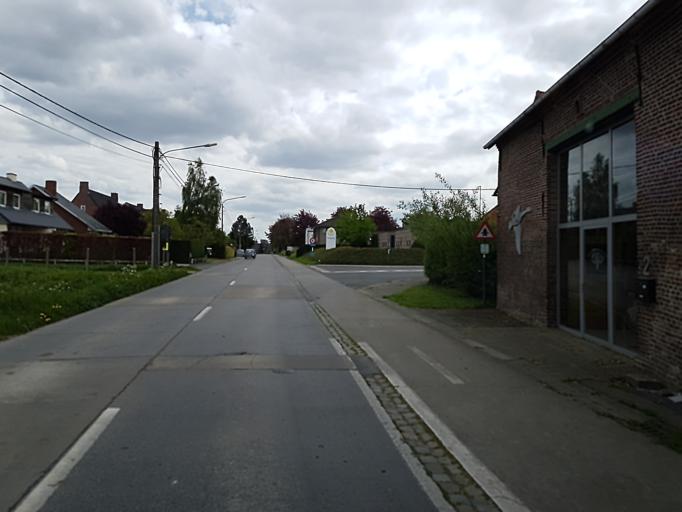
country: BE
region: Flanders
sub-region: Provincie West-Vlaanderen
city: Avelgem
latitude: 50.7839
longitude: 3.4474
